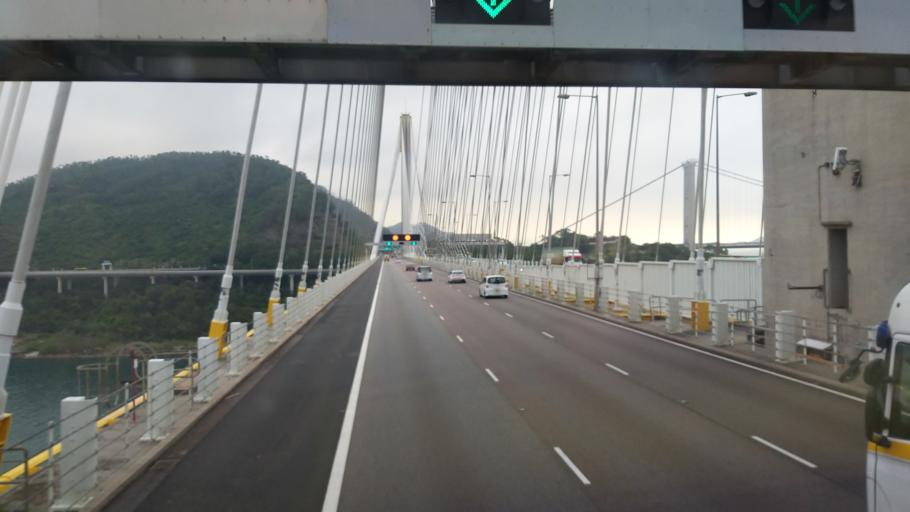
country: HK
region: Tsuen Wan
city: Tsuen Wan
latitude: 22.3642
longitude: 114.0798
